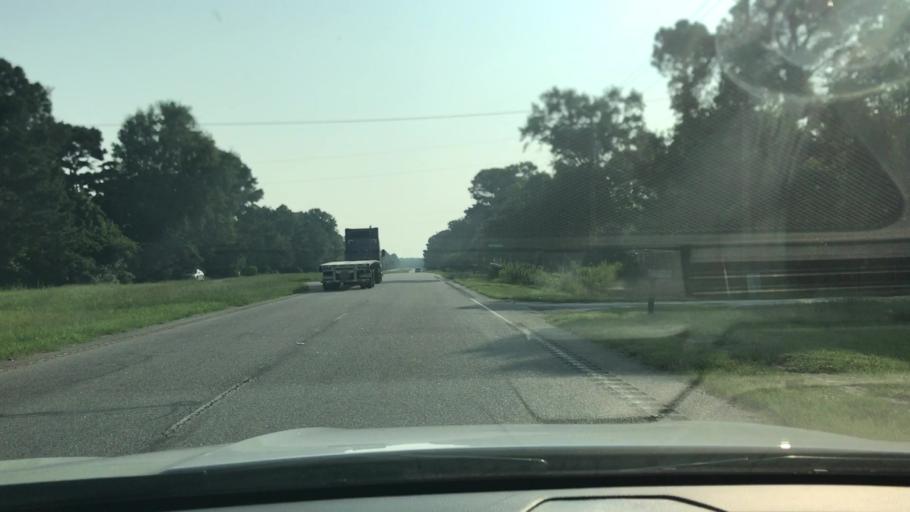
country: US
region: South Carolina
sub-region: Charleston County
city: Awendaw
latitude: 33.0488
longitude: -79.5610
